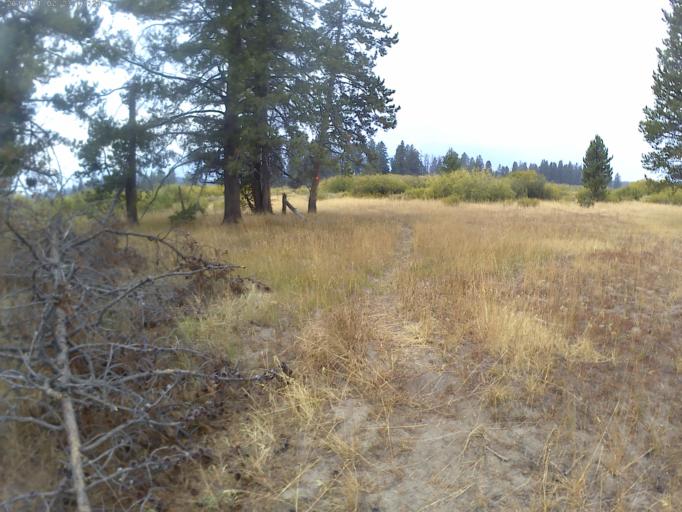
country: US
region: Wyoming
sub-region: Teton County
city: Moose Wilson Road
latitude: 43.8881
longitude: -110.6128
